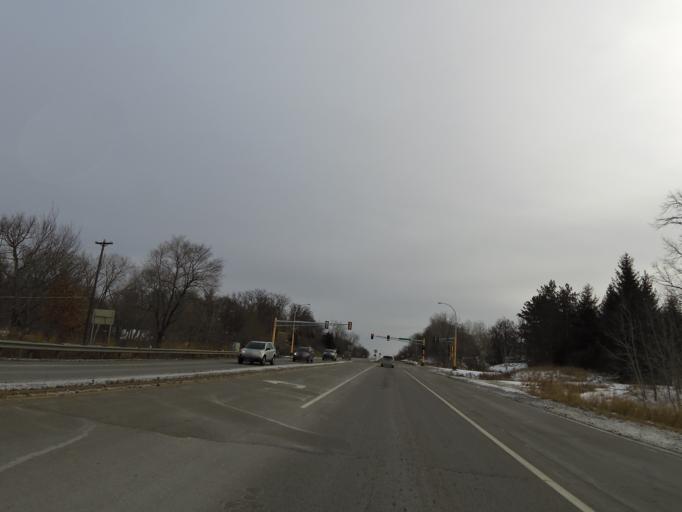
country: US
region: Minnesota
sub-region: Scott County
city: Prior Lake
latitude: 44.7251
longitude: -93.4049
